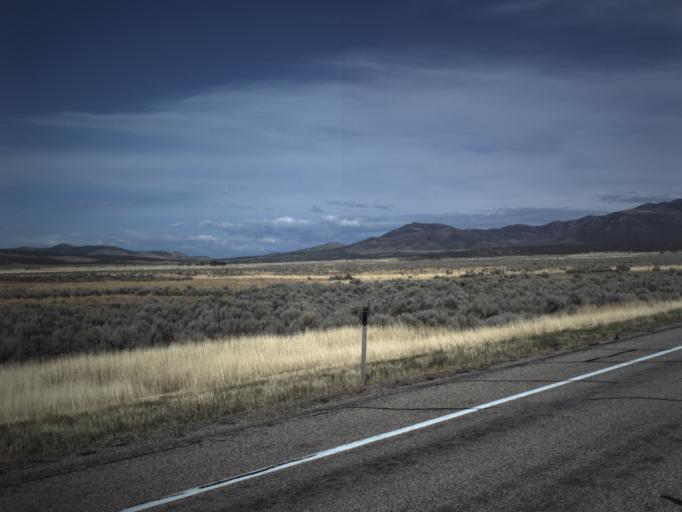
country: US
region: Utah
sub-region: Millard County
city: Fillmore
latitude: 39.1143
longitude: -112.2861
